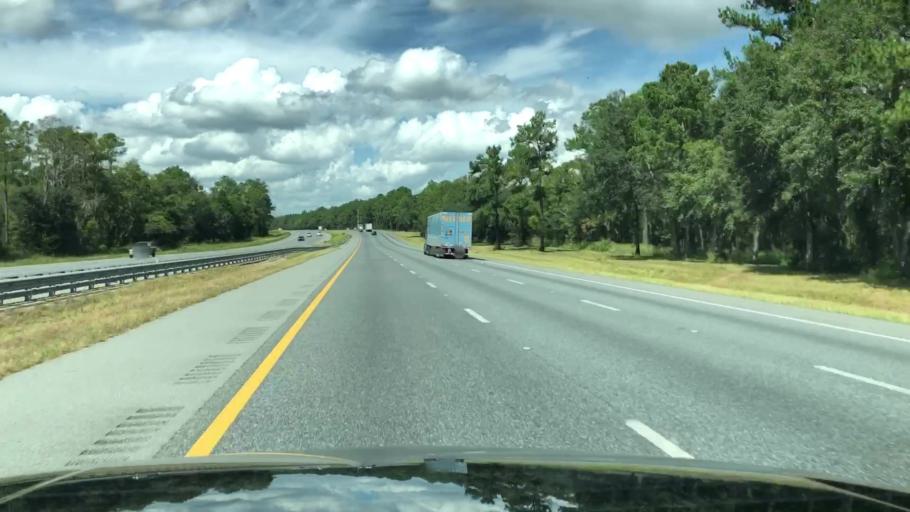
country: US
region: Florida
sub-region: Suwannee County
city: Wellborn
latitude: 30.3526
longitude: -82.8371
